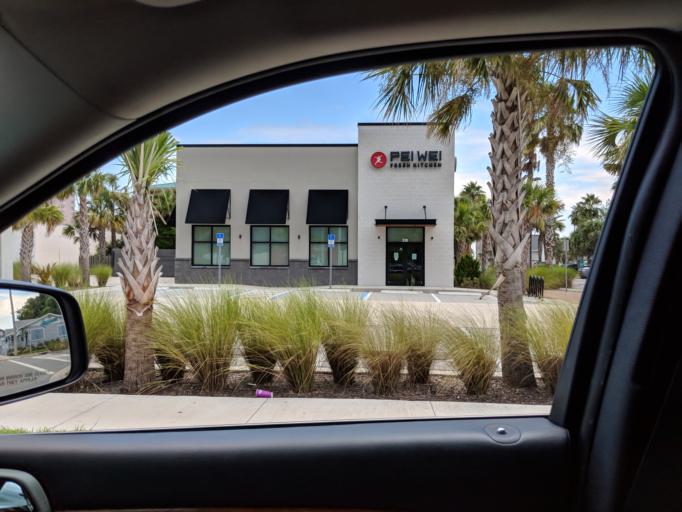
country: US
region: Florida
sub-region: Duval County
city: Jacksonville Beach
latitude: 30.2857
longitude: -81.3927
